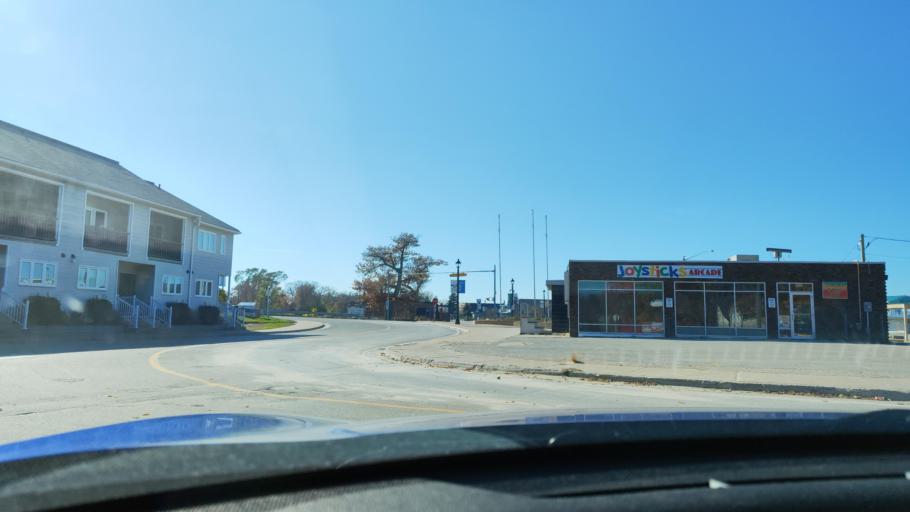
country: CA
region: Ontario
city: Wasaga Beach
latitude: 44.5242
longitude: -80.0174
